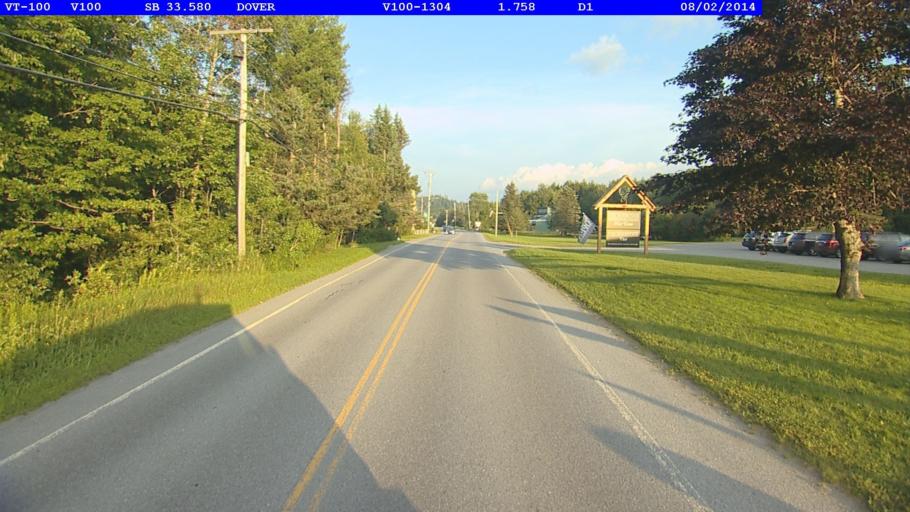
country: US
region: Vermont
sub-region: Windham County
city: Dover
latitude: 42.9442
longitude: -72.8624
